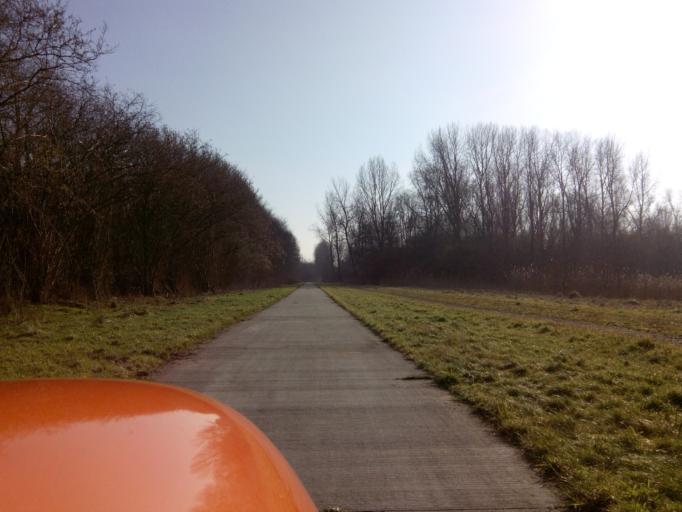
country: NL
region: Flevoland
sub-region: Gemeente Zeewolde
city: Zeewolde
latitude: 52.3072
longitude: 5.4990
